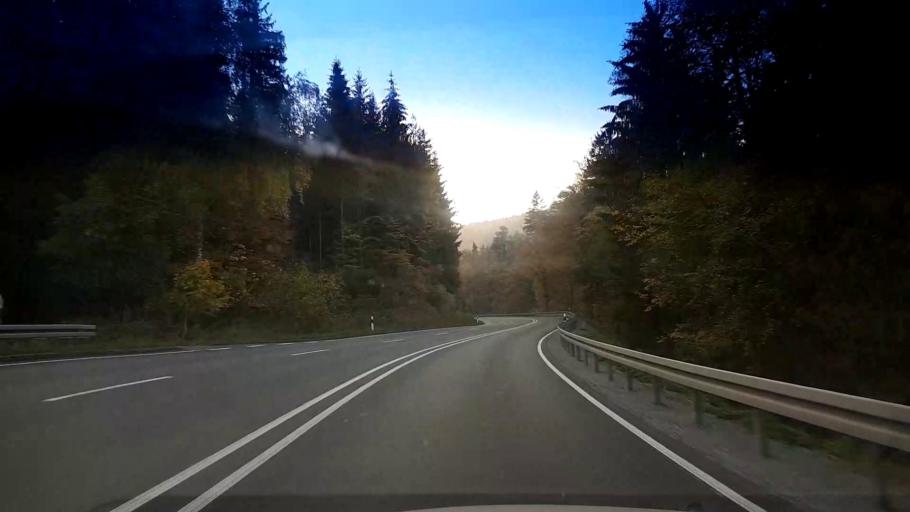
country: DE
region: Bavaria
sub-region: Upper Franconia
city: Bischofsgrun
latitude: 50.0418
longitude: 11.7339
